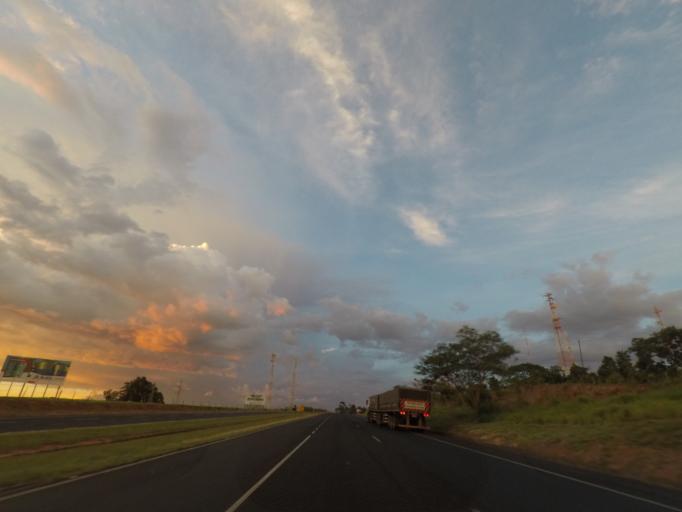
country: BR
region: Minas Gerais
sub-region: Uberaba
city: Uberaba
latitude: -19.5870
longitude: -48.0302
